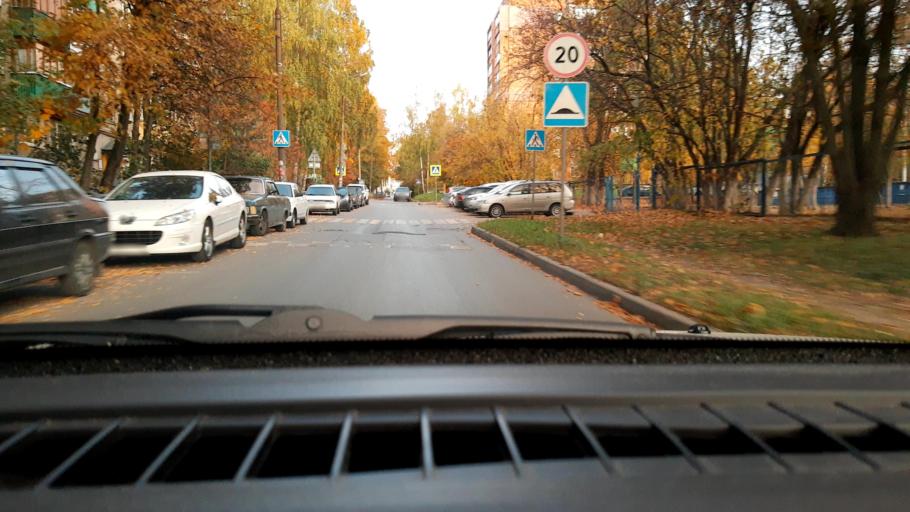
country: RU
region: Nizjnij Novgorod
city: Nizhniy Novgorod
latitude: 56.2334
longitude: 43.9574
